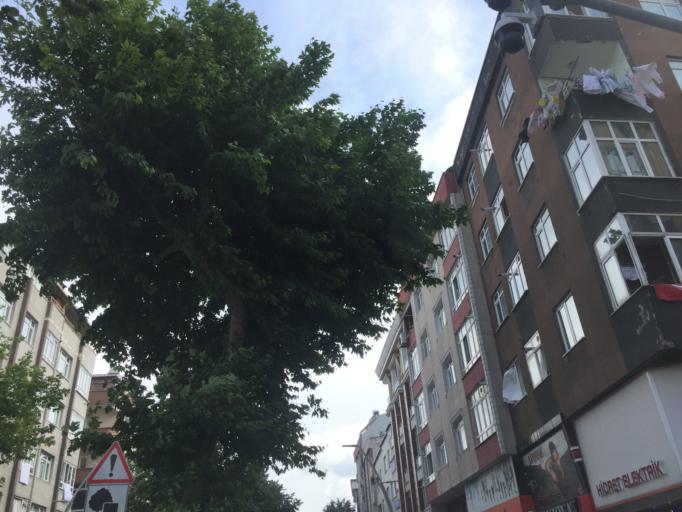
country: TR
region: Istanbul
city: Zeytinburnu
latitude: 41.0031
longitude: 28.9043
